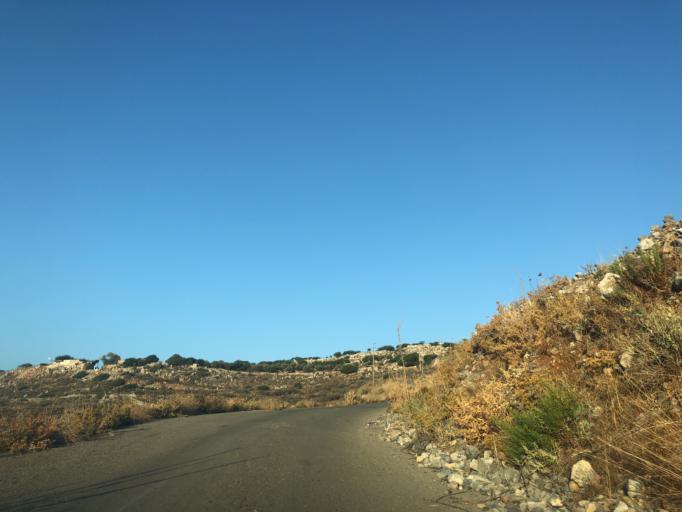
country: GR
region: Crete
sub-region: Nomos Rethymnis
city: Atsipopoulon
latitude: 35.3593
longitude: 24.3919
